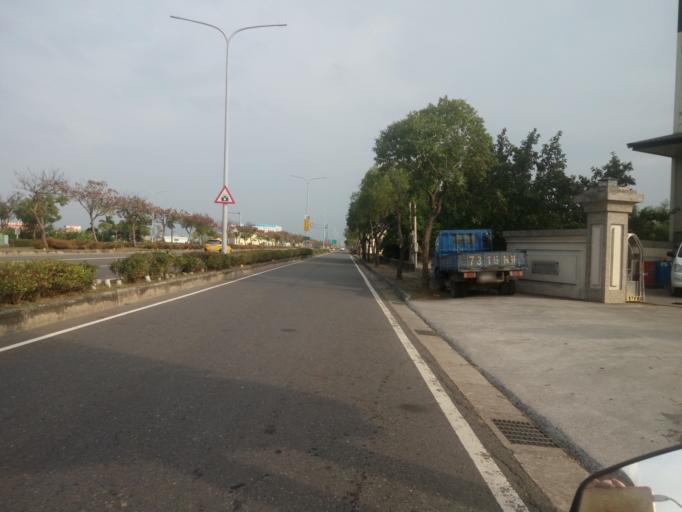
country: TW
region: Taiwan
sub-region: Chiayi
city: Jiayi Shi
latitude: 23.4877
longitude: 120.4004
